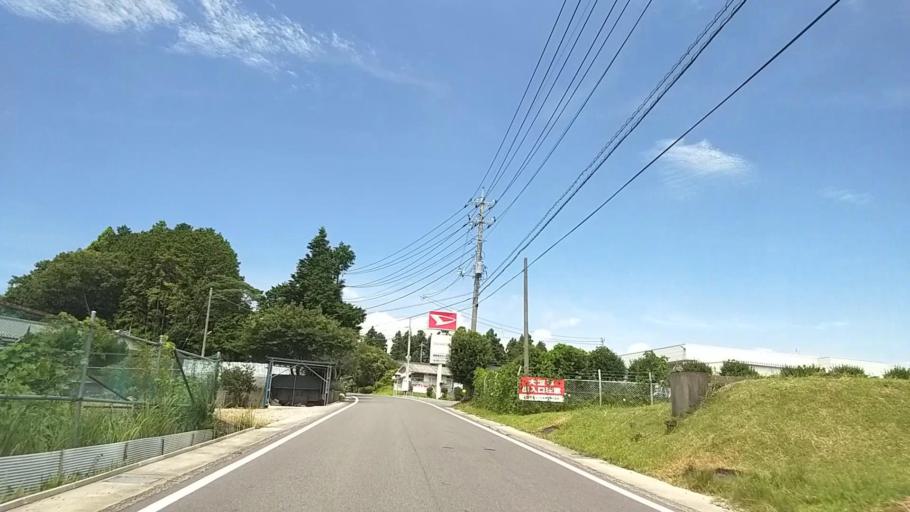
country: JP
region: Shizuoka
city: Gotemba
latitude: 35.2456
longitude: 138.8548
